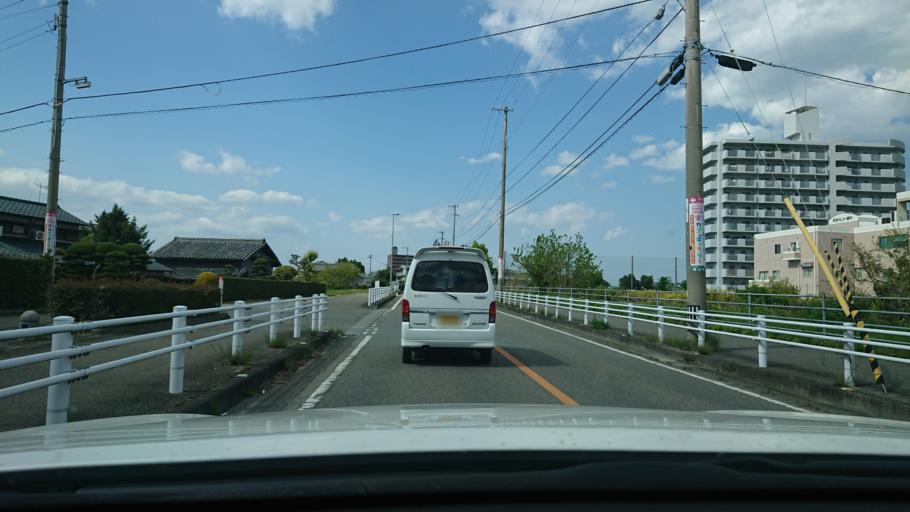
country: JP
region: Tokushima
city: Komatsushimacho
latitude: 34.0143
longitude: 134.5558
